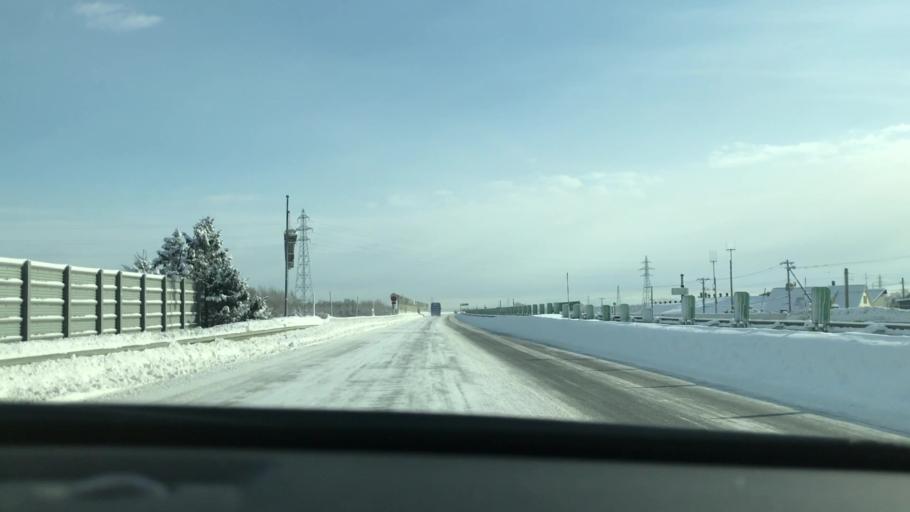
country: JP
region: Hokkaido
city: Ebetsu
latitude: 43.0911
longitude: 141.4629
